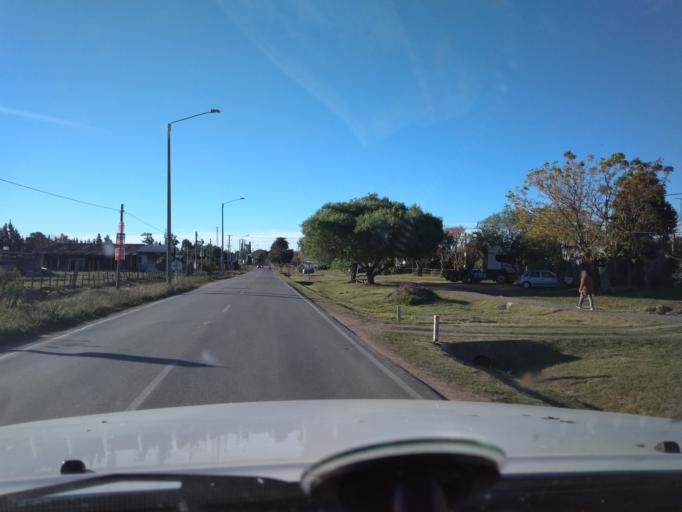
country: UY
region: Canelones
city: San Ramon
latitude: -34.3018
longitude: -55.9580
